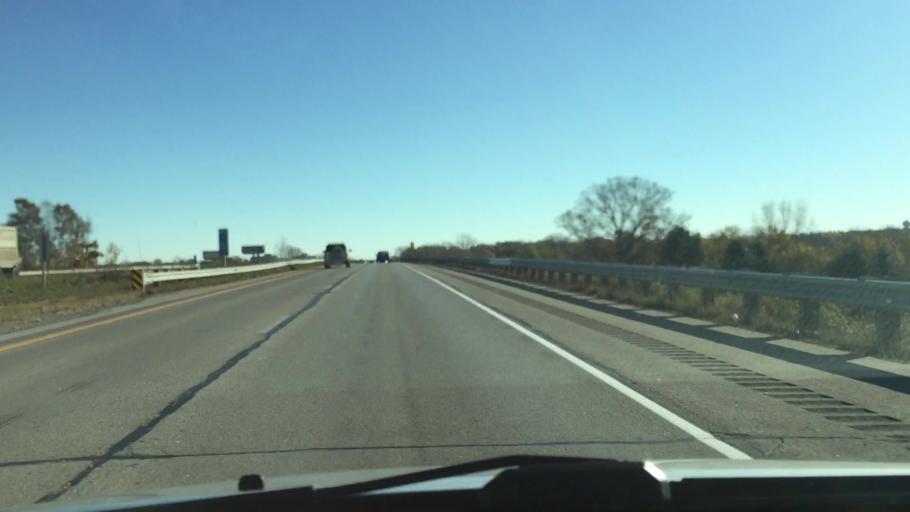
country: US
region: Wisconsin
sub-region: Outagamie County
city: Appleton
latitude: 44.2989
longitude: -88.4375
